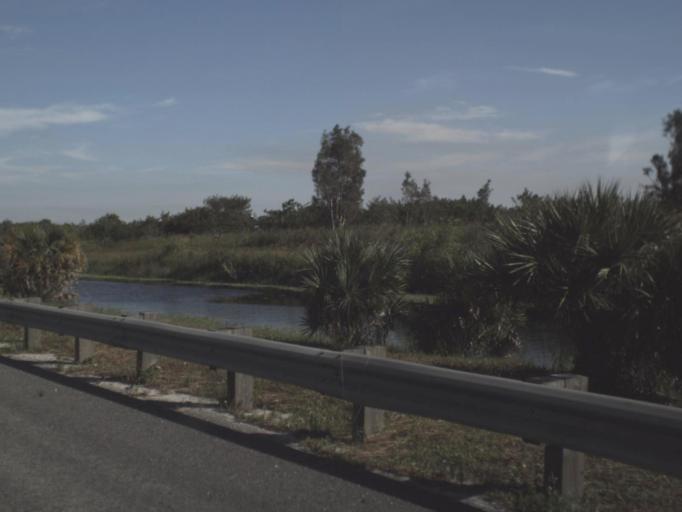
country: US
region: Florida
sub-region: Glades County
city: Moore Haven
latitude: 26.7537
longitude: -81.0449
